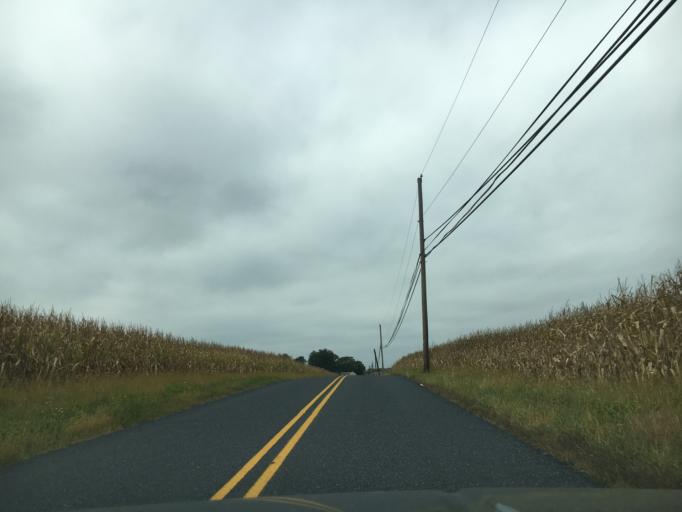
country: US
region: Pennsylvania
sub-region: Northampton County
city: Bath
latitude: 40.6973
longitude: -75.3977
